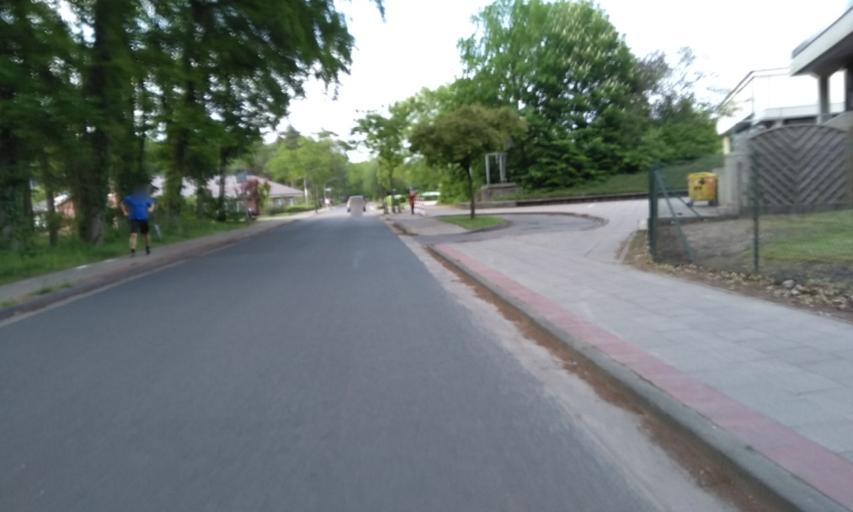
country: DE
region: Lower Saxony
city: Harsefeld
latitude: 53.4447
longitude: 9.4918
